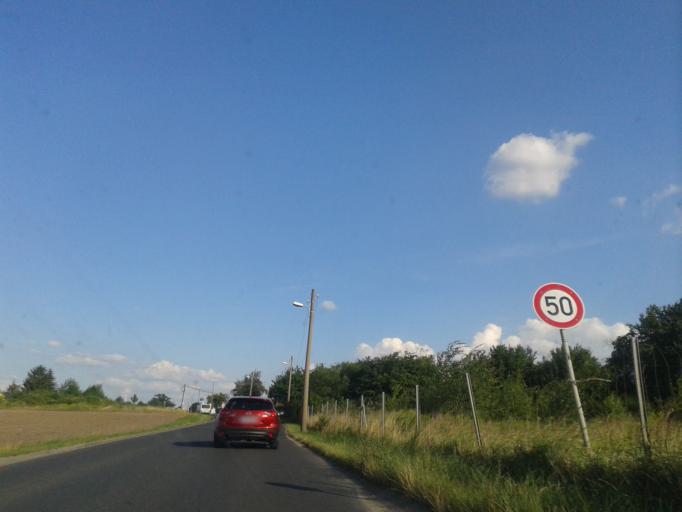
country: DE
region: Saxony
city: Radebeul
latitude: 51.0942
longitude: 13.6667
